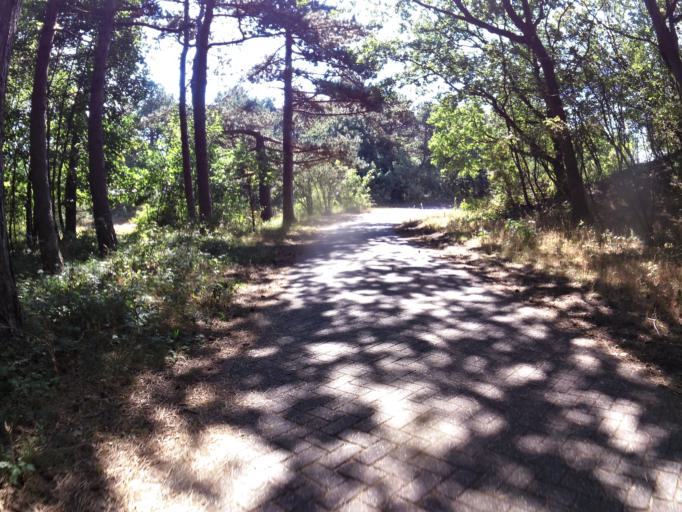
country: NL
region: North Holland
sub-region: Gemeente Beverwijk
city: Beverwijk
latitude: 52.5166
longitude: 4.6142
